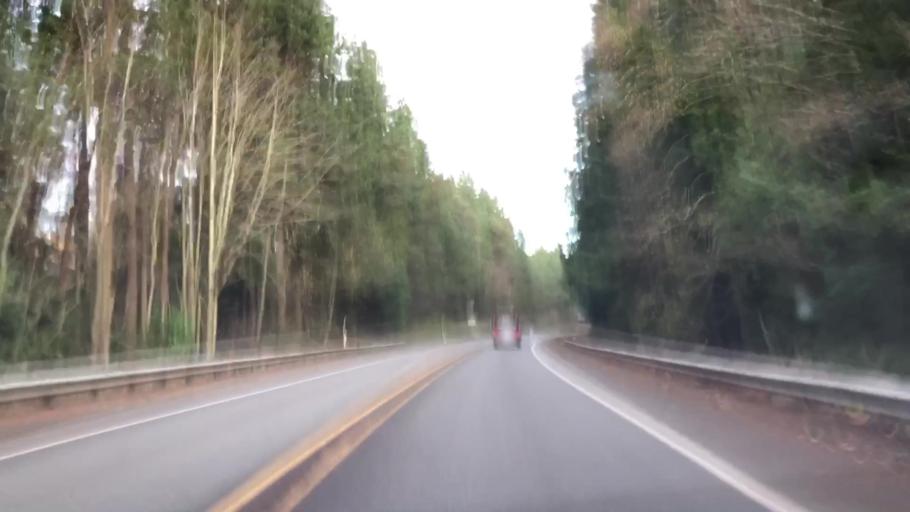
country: US
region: Washington
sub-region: Kitsap County
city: Bainbridge Island
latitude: 47.6479
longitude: -122.5227
